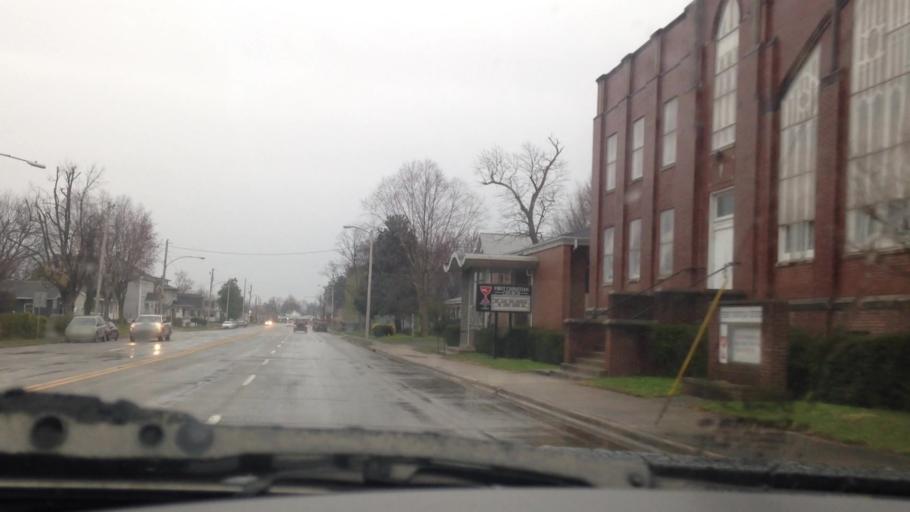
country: US
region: Illinois
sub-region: Massac County
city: Metropolis
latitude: 37.1490
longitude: -88.7281
